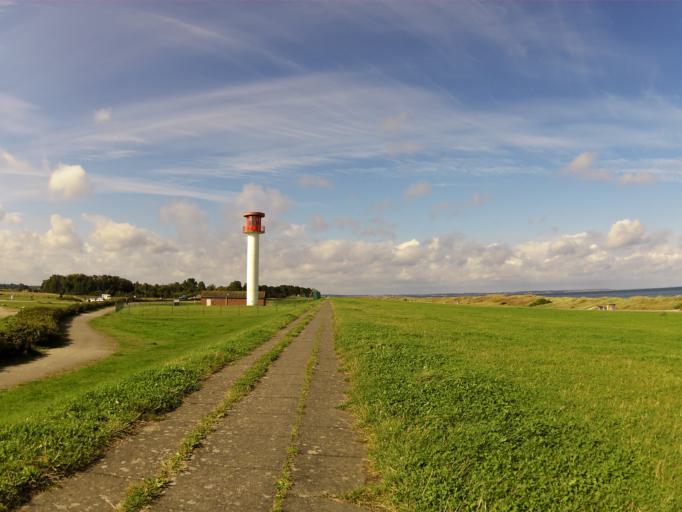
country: DE
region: Schleswig-Holstein
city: Wendtorf
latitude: 54.4343
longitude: 10.3185
